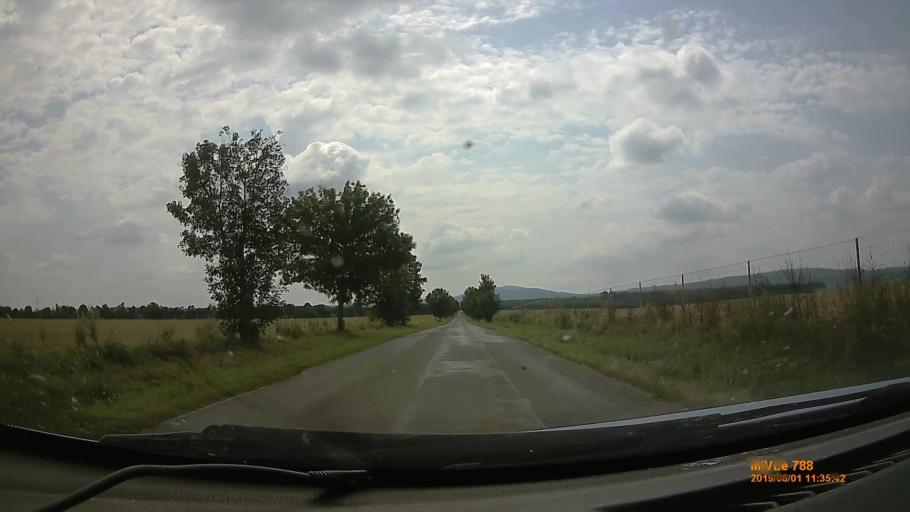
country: HU
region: Baranya
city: Siklos
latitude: 45.9247
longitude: 18.3699
